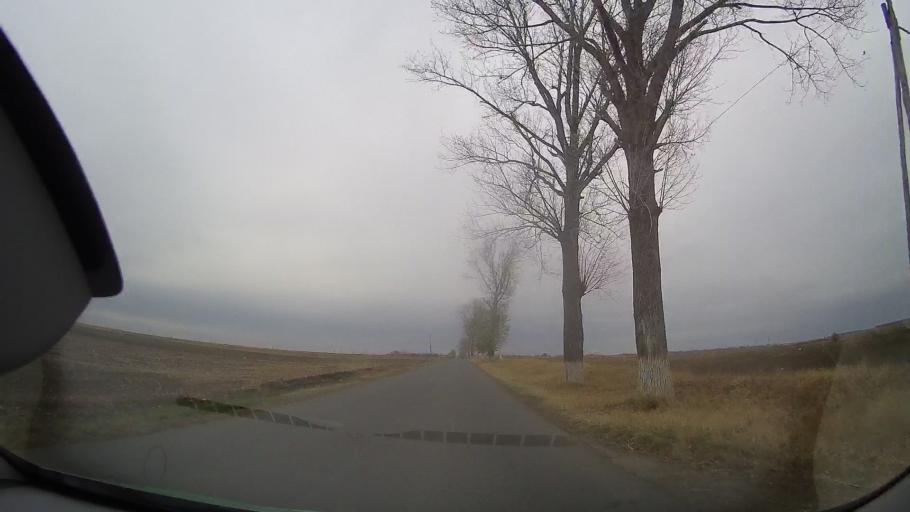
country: RO
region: Braila
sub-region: Comuna Budesti
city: Tataru
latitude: 44.8676
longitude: 27.4275
